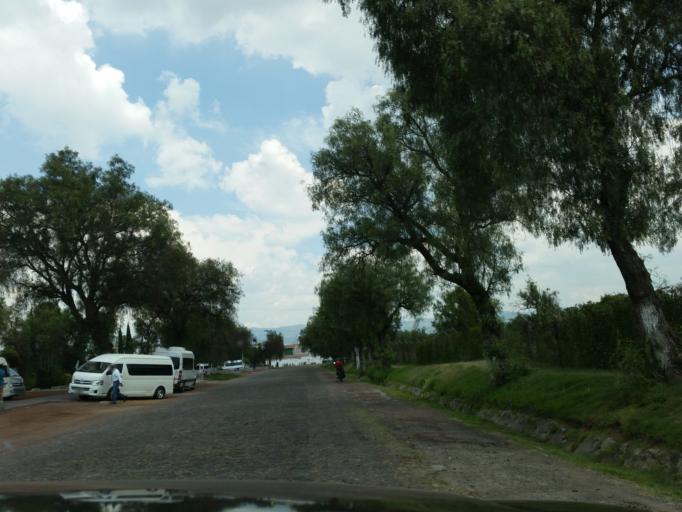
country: MX
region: Morelos
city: San Martin de las Piramides
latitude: 19.6993
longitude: -98.8397
